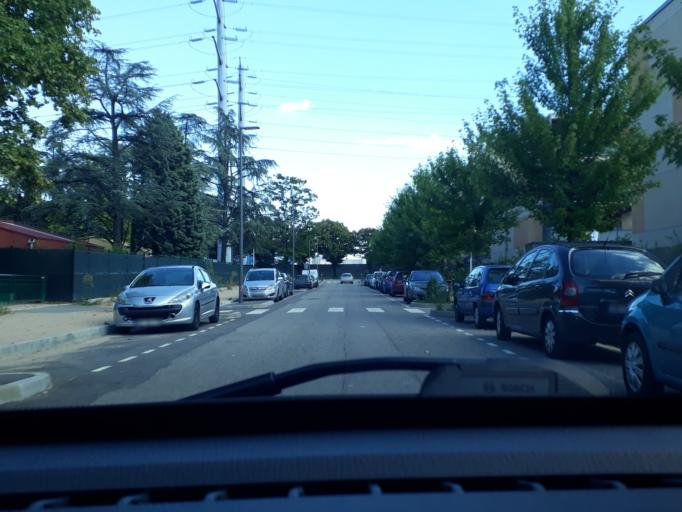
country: FR
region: Rhone-Alpes
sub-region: Departement du Rhone
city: Venissieux
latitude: 45.7029
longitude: 4.8997
